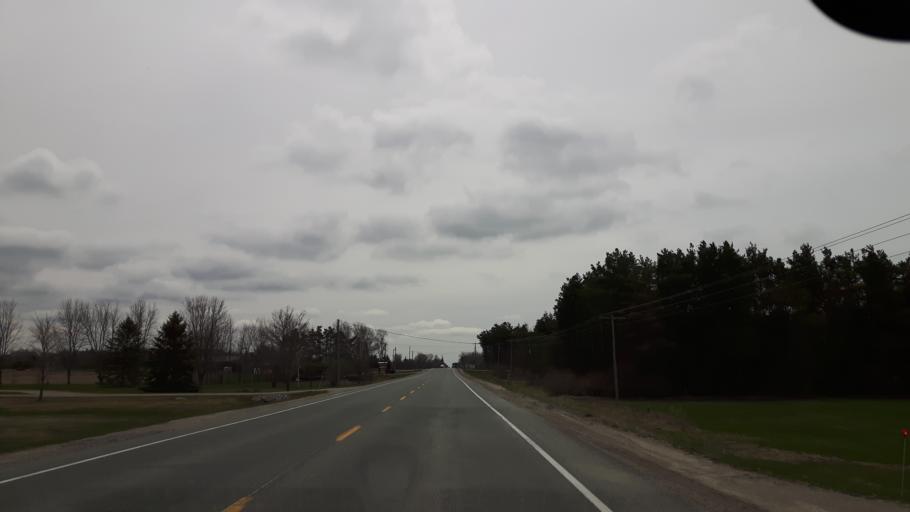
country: CA
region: Ontario
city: Goderich
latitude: 43.7102
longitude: -81.7057
